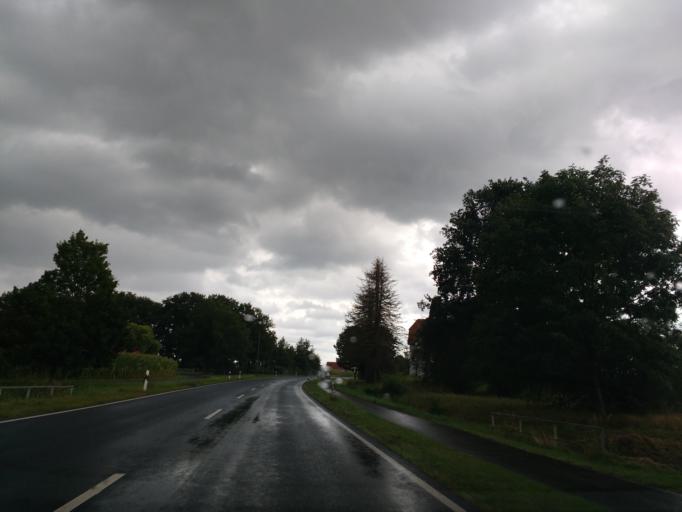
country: DE
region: Lower Saxony
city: Glandorf
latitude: 52.0921
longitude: 7.9672
